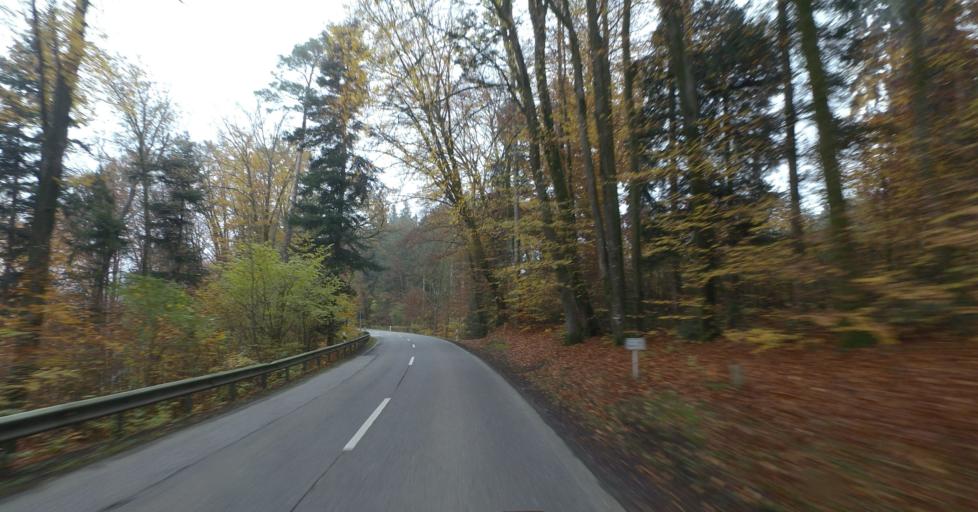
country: DE
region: Bavaria
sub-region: Upper Bavaria
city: Seeon-Seebruck
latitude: 47.9628
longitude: 12.5131
